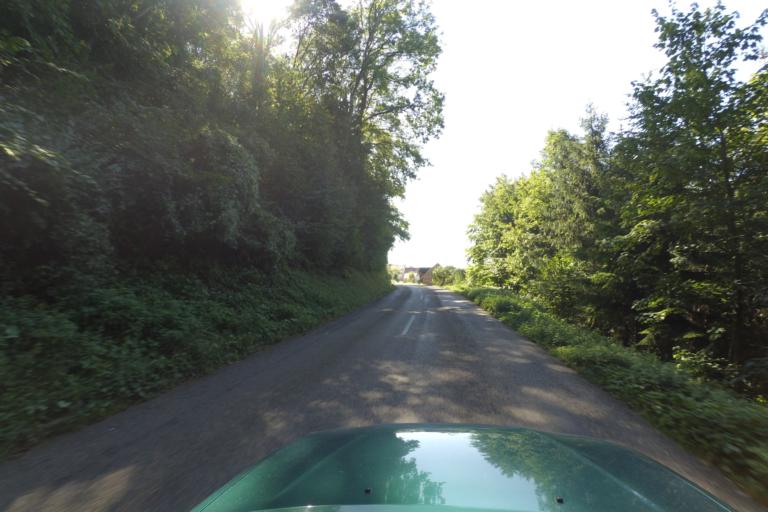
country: DE
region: Baden-Wuerttemberg
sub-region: Regierungsbezirk Stuttgart
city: Langenburg
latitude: 49.2556
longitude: 9.8535
